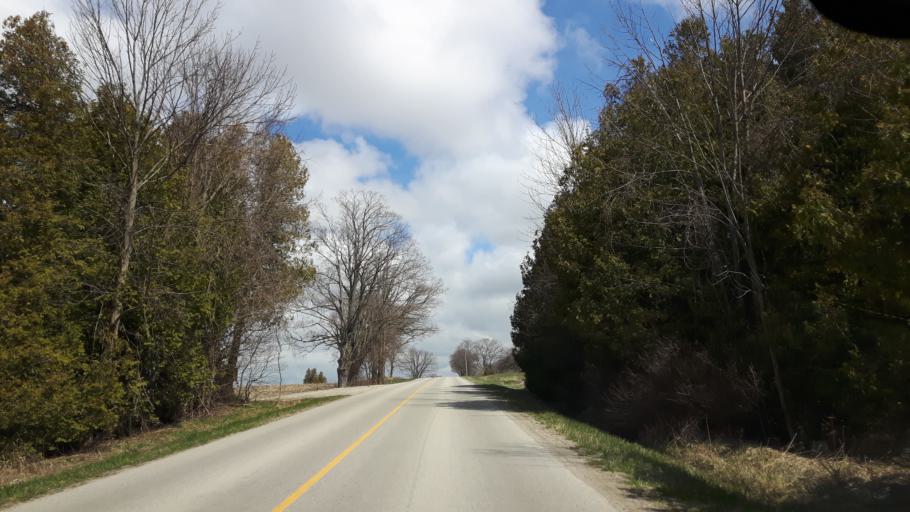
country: CA
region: Ontario
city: Goderich
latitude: 43.6585
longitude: -81.6846
